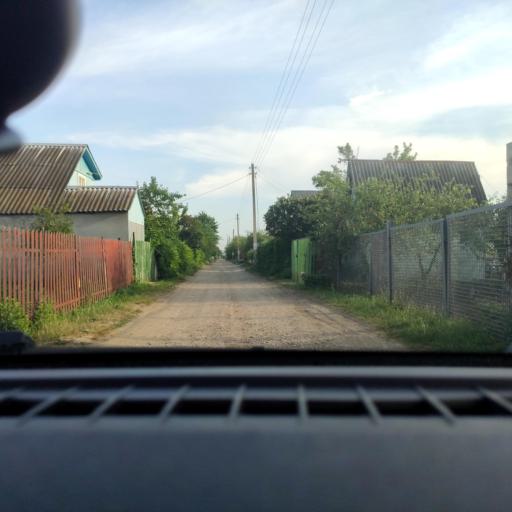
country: RU
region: Samara
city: Tol'yatti
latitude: 53.5927
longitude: 49.3238
